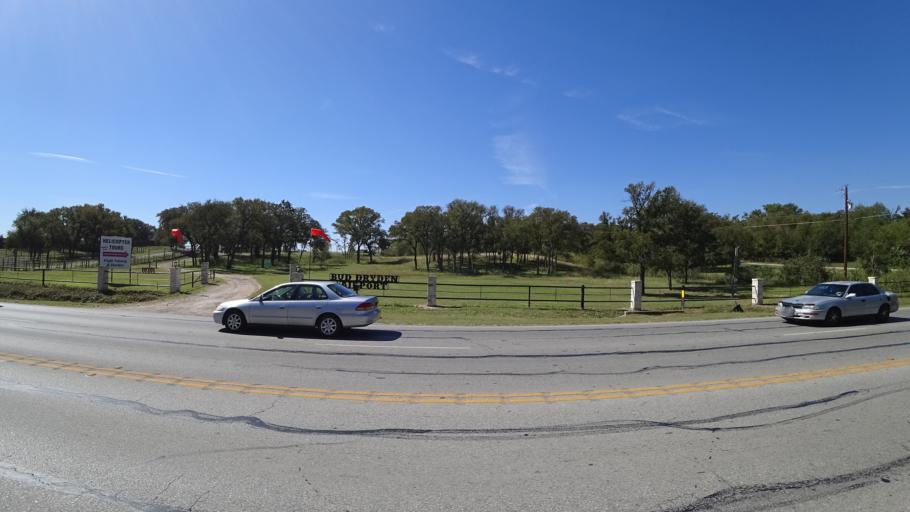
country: US
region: Texas
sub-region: Travis County
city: Hornsby Bend
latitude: 30.2644
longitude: -97.6231
